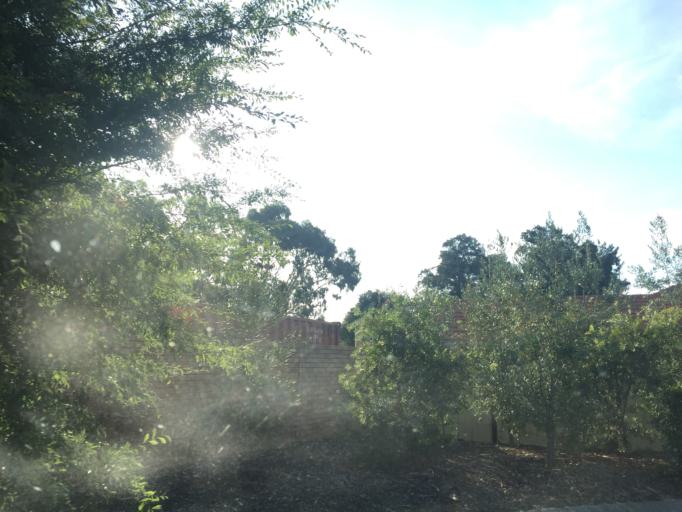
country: AU
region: Western Australia
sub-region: City of Cockburn
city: City of Cockburn
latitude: -32.0922
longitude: 115.8411
